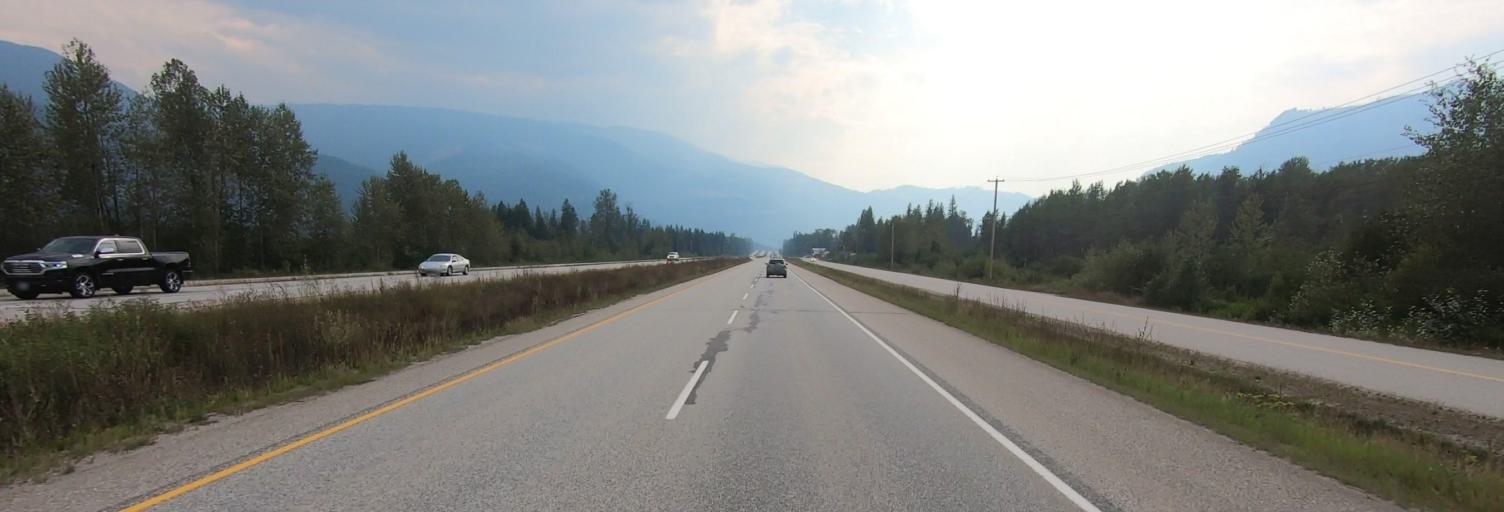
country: CA
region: British Columbia
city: Sicamous
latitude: 50.9214
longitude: -118.7975
